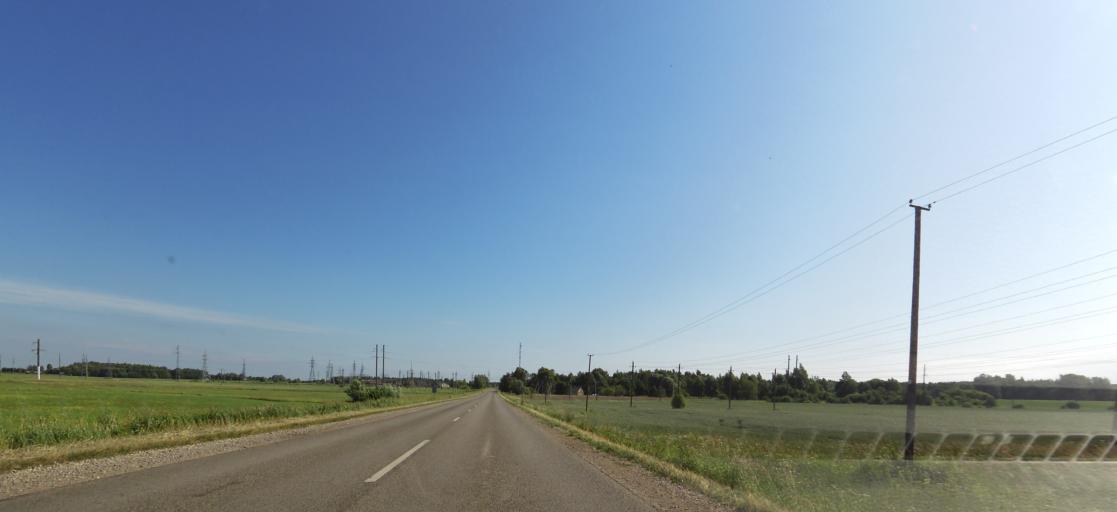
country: LT
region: Panevezys
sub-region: Birzai
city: Birzai
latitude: 56.2330
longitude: 24.8175
